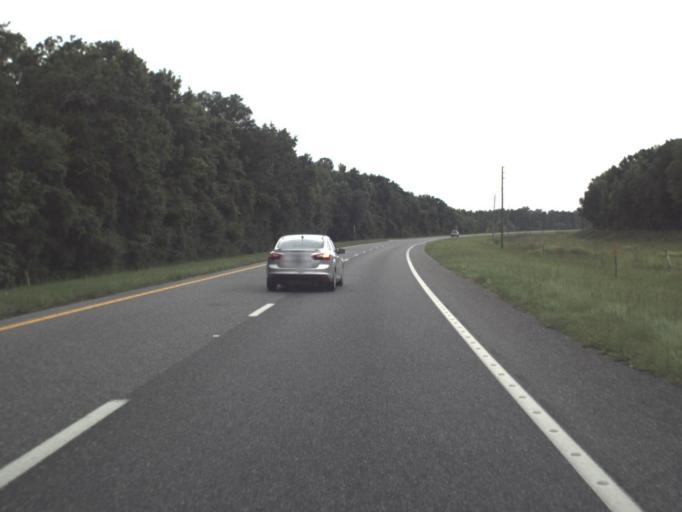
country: US
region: Florida
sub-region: Levy County
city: Inglis
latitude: 29.1851
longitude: -82.6791
